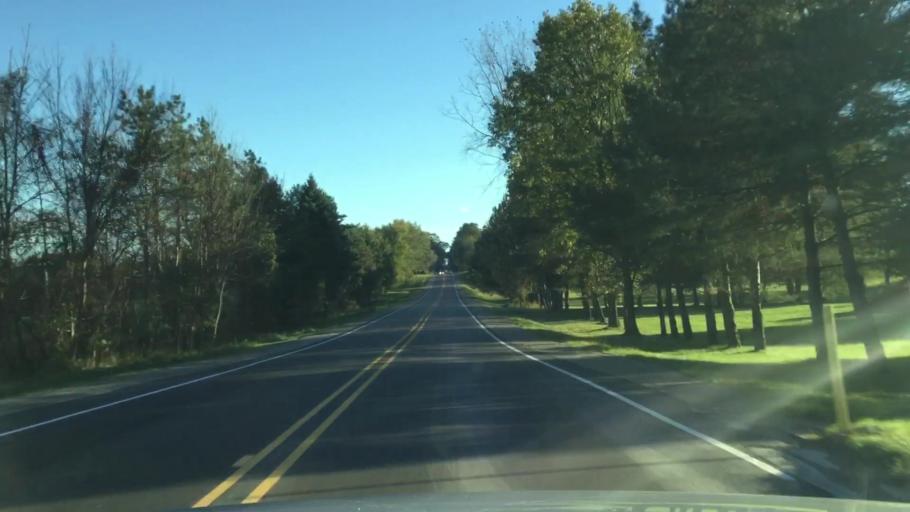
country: US
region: Michigan
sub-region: Lapeer County
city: Almont
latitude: 42.9237
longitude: -83.1437
